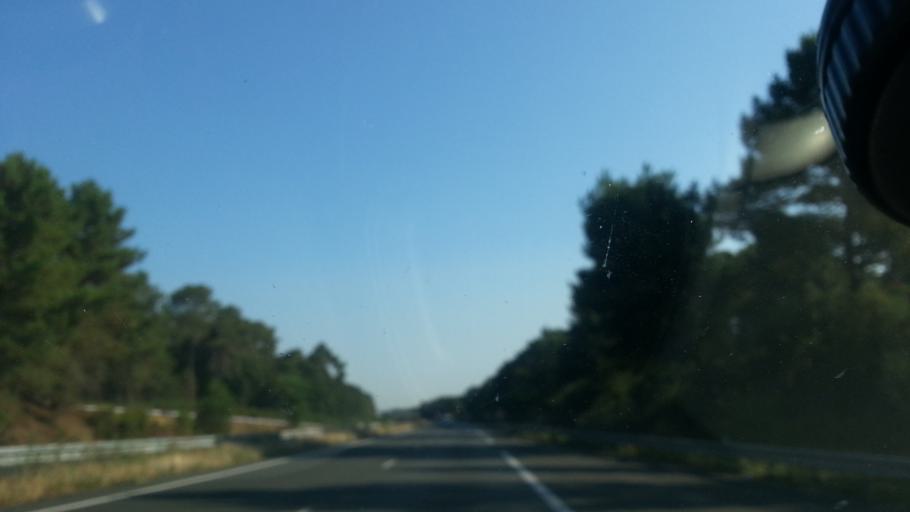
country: FR
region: Poitou-Charentes
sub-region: Departement de la Vienne
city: Chatellerault
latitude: 46.7951
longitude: 0.5110
